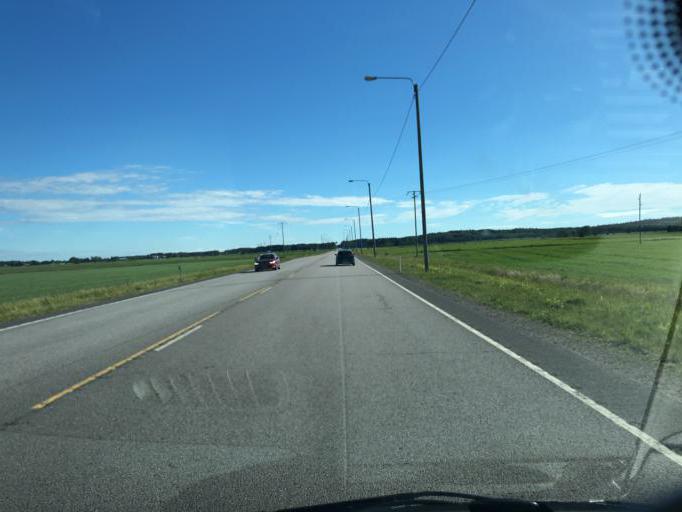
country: FI
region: Uusimaa
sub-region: Loviisa
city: Lapinjaervi
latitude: 60.6608
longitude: 26.2442
